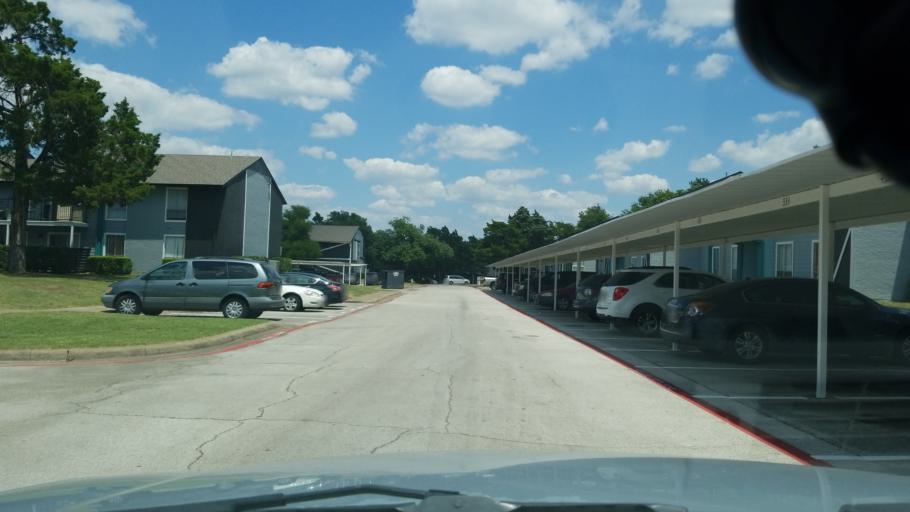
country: US
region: Texas
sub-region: Dallas County
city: Cockrell Hill
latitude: 32.6886
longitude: -96.8632
